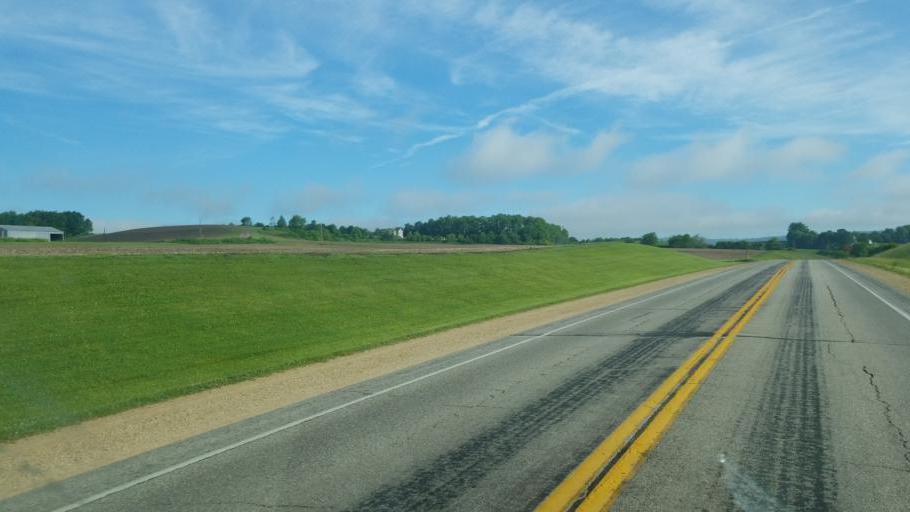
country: US
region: Wisconsin
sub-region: Vernon County
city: Hillsboro
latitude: 43.6418
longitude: -90.3572
